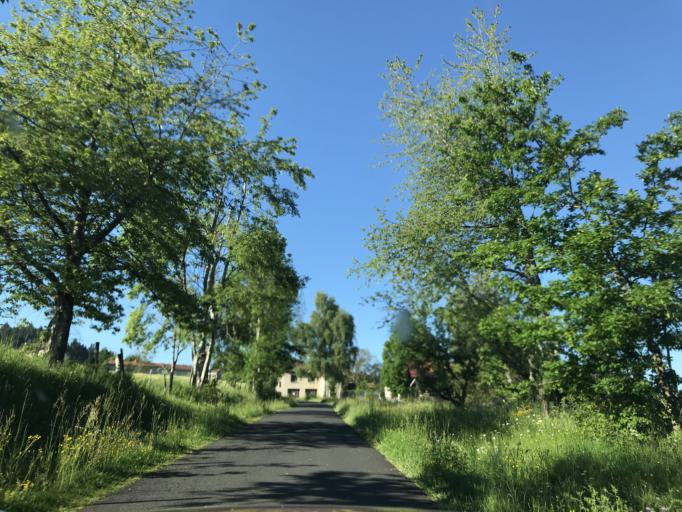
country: FR
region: Auvergne
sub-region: Departement du Puy-de-Dome
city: Job
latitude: 45.6382
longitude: 3.6765
